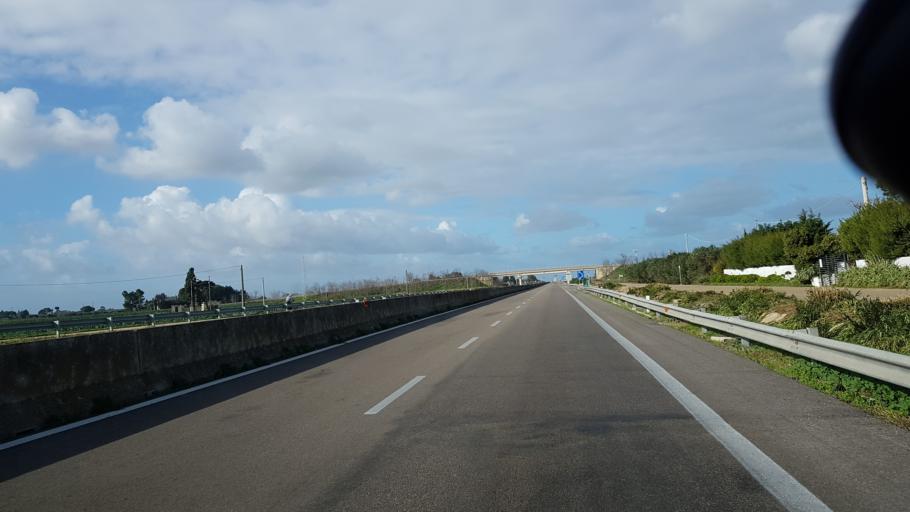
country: IT
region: Apulia
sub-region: Provincia di Brindisi
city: Brindisi
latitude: 40.6875
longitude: 17.8278
